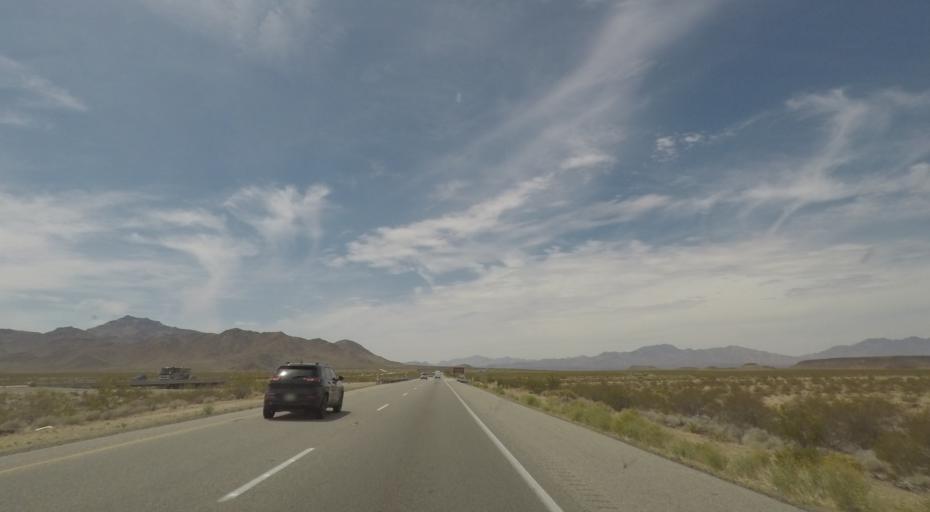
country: US
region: California
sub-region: San Bernardino County
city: Needles
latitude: 34.8023
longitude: -115.3059
